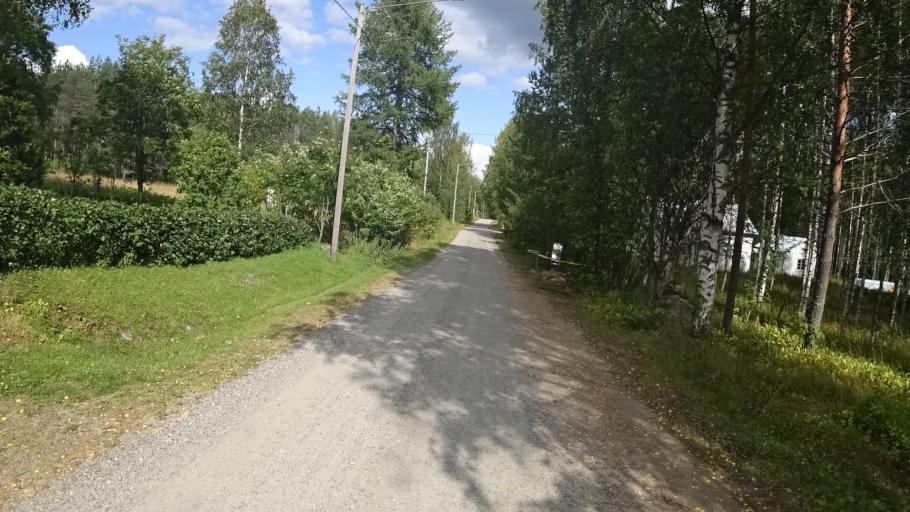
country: FI
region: North Karelia
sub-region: Joensuu
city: Ilomantsi
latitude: 62.6342
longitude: 31.2777
